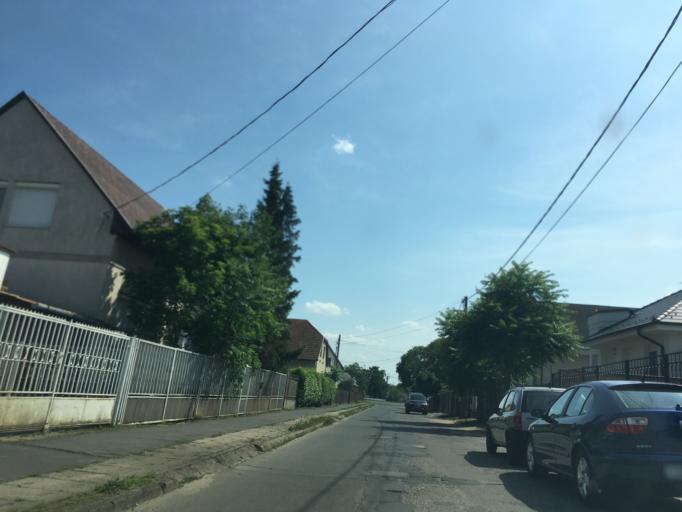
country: HU
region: Hajdu-Bihar
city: Debrecen
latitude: 47.5484
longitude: 21.6531
